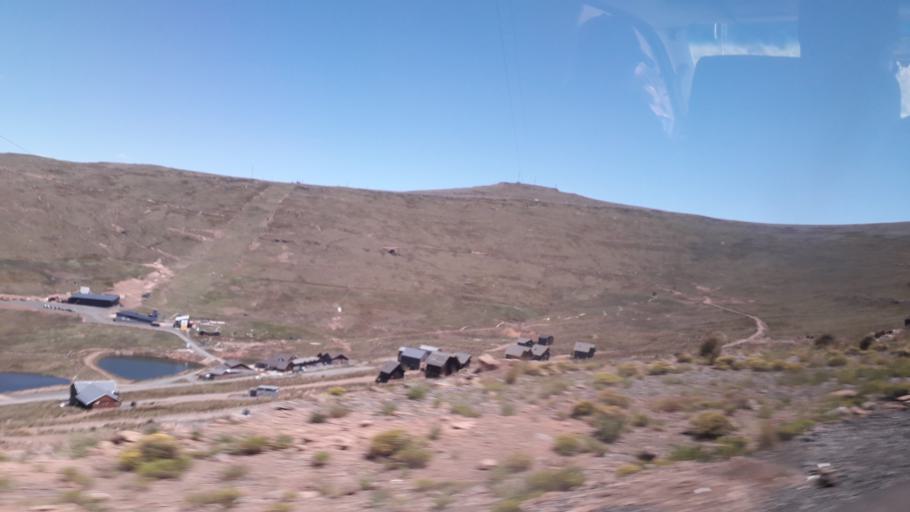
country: ZA
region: Orange Free State
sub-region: Thabo Mofutsanyana District Municipality
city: Phuthaditjhaba
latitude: -28.8253
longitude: 28.7313
